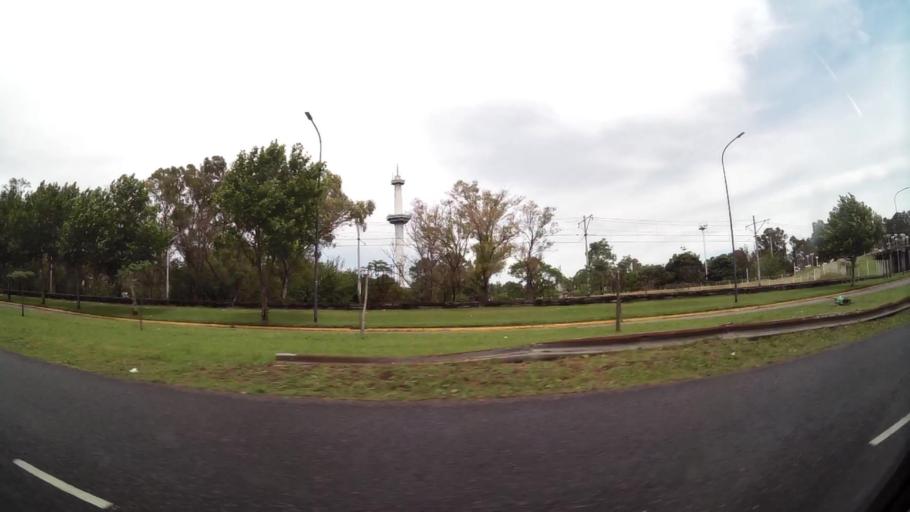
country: AR
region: Buenos Aires F.D.
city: Villa Lugano
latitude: -34.6682
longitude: -58.4537
